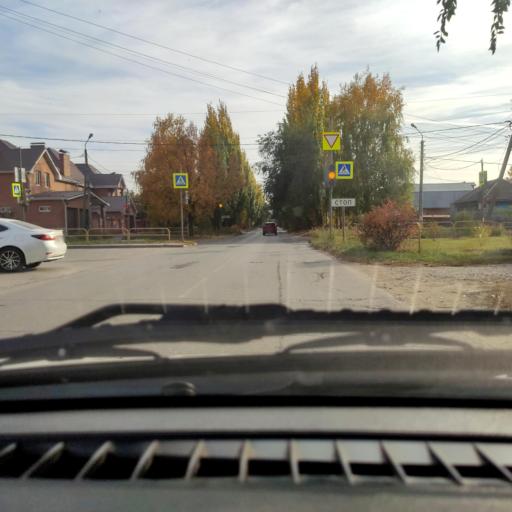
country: RU
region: Samara
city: Tol'yatti
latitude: 53.5365
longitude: 49.4170
